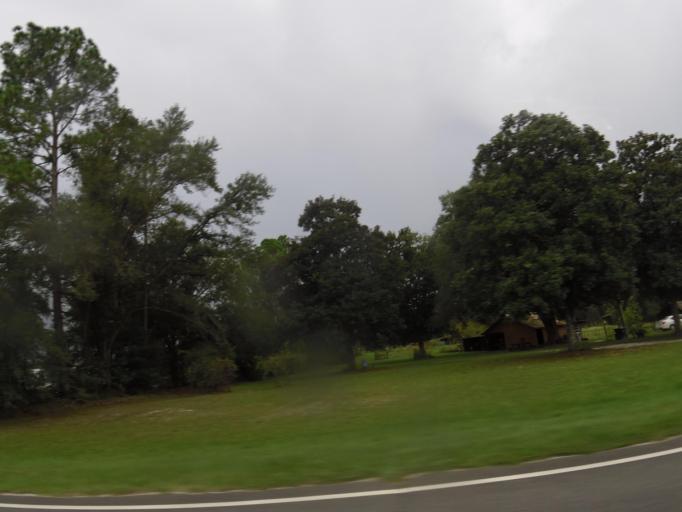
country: US
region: Florida
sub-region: Baker County
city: Macclenny
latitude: 30.4147
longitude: -82.1970
